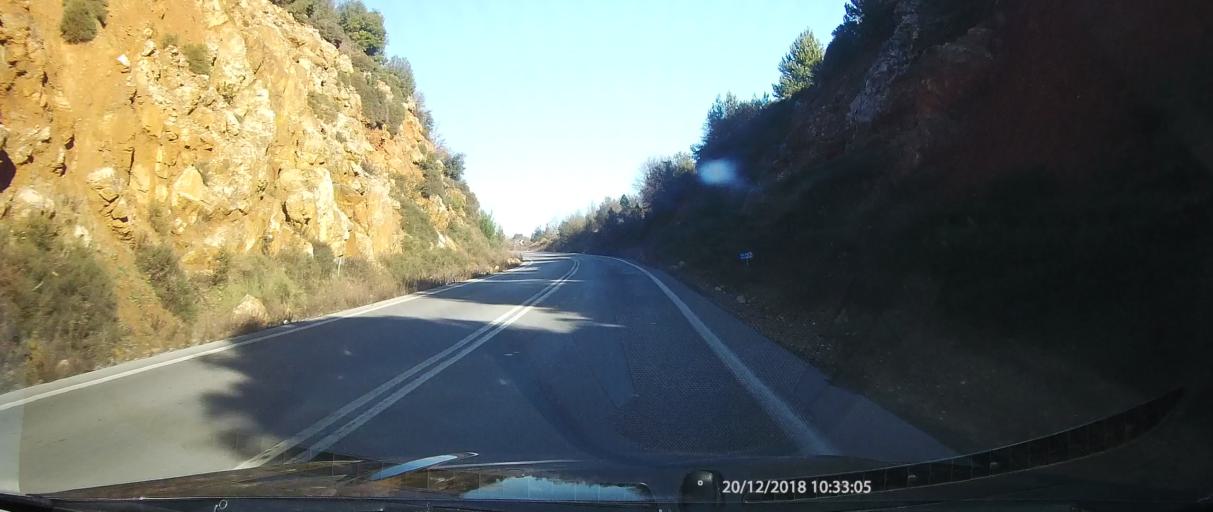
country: GR
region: Peloponnese
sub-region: Nomos Lakonias
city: Kariai
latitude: 37.3342
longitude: 22.4180
